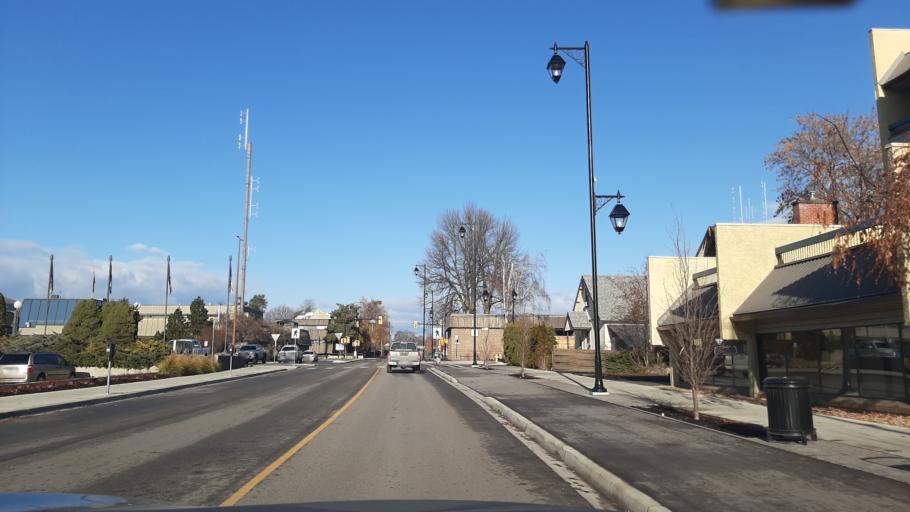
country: CA
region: British Columbia
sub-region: Regional District of North Okanagan
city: Vernon
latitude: 50.2662
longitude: -119.2707
